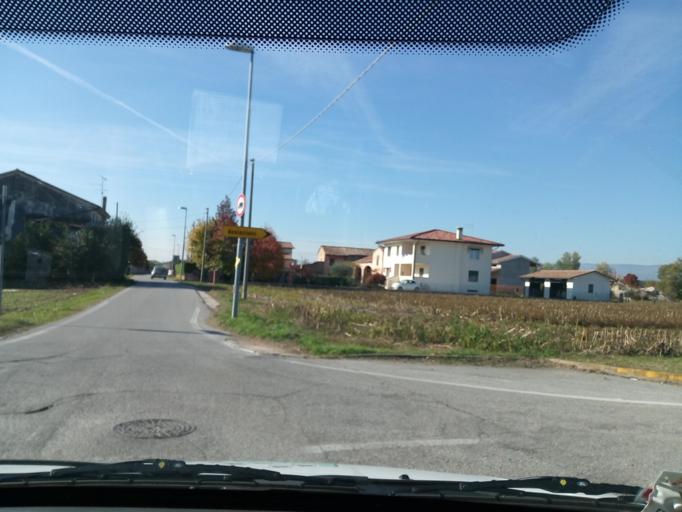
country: IT
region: Veneto
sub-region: Provincia di Vicenza
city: Rossano Veneto
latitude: 45.7048
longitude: 11.8203
